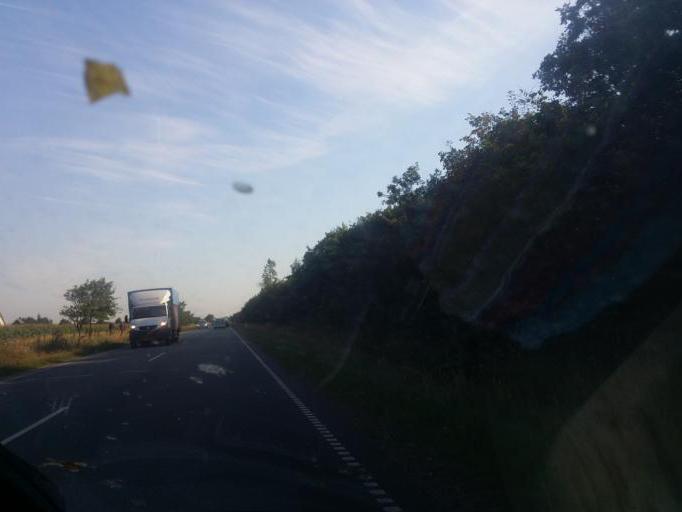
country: DK
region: South Denmark
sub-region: Esbjerg Kommune
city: Ribe
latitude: 55.3078
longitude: 8.7471
